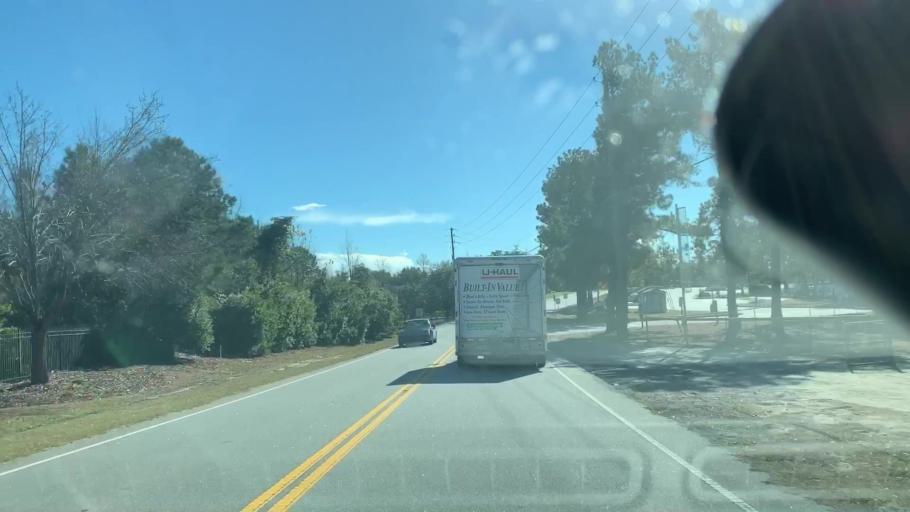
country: US
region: South Carolina
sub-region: Richland County
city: Woodfield
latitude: 34.0850
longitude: -80.8904
